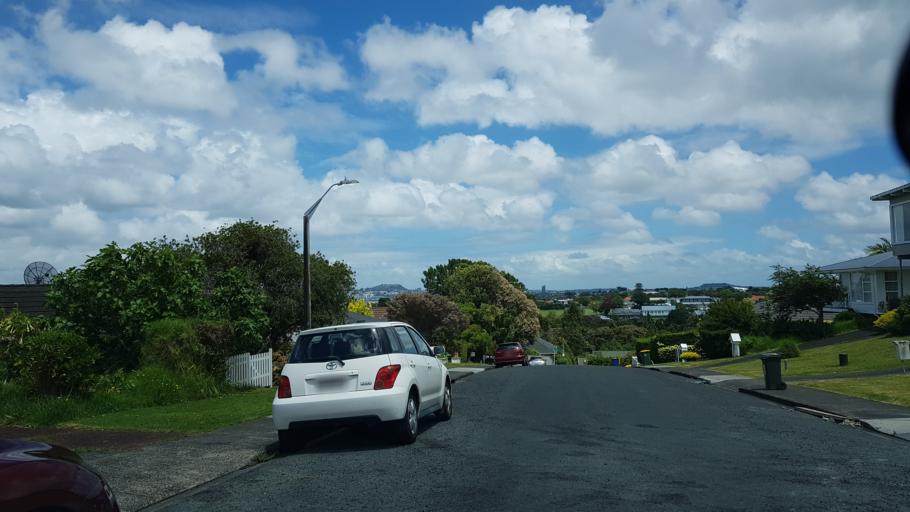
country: NZ
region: Auckland
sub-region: Auckland
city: North Shore
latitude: -36.8023
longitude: 174.7347
